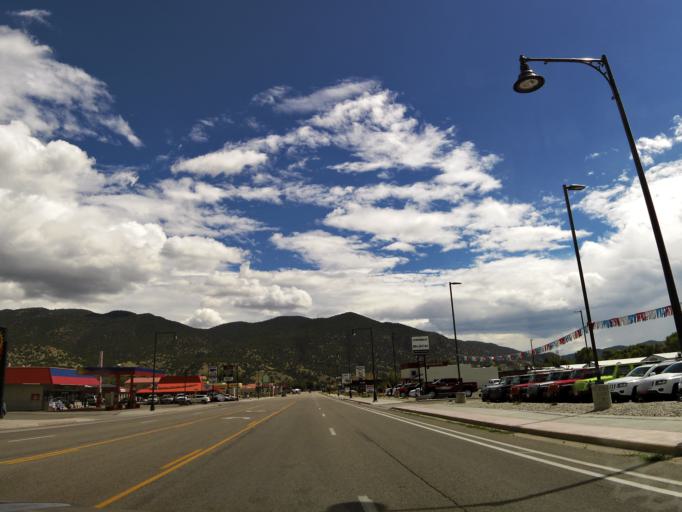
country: US
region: Colorado
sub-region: Chaffee County
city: Salida
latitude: 38.5240
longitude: -105.9923
